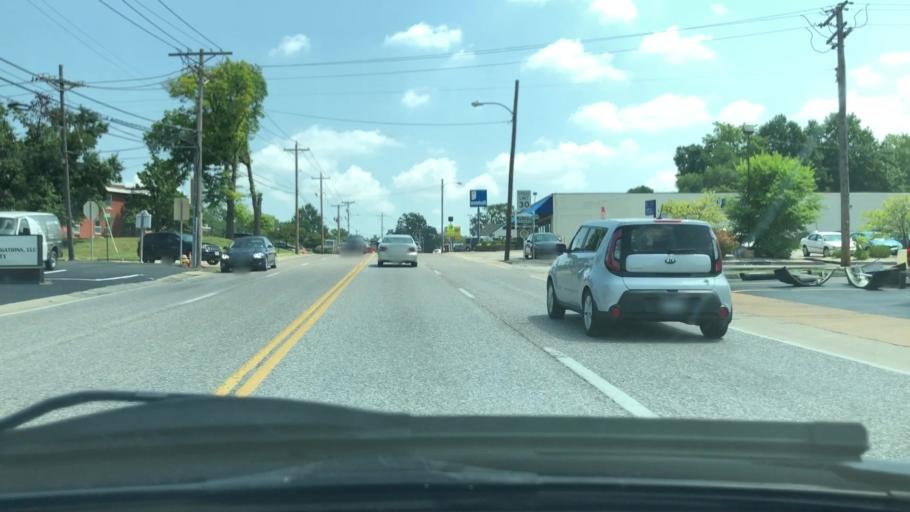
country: US
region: Missouri
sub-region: Saint Louis County
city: Brentwood
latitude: 38.6118
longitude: -90.3567
